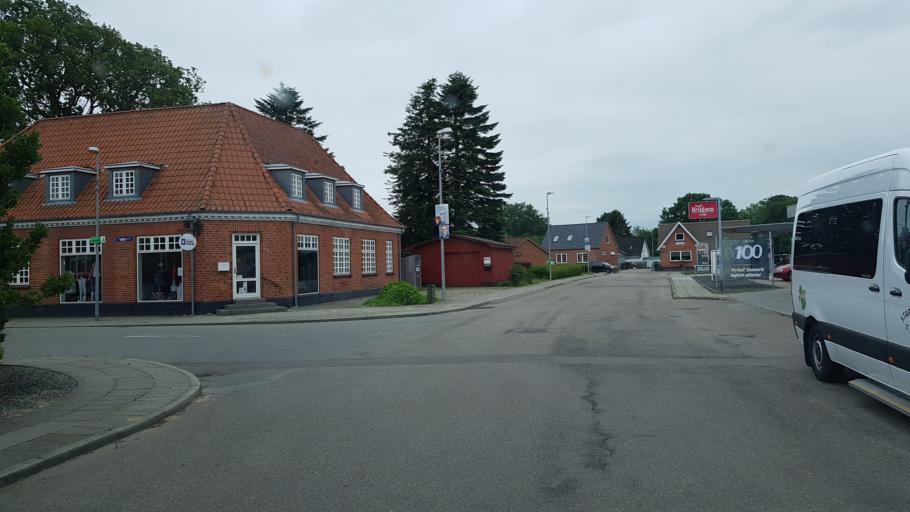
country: DK
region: South Denmark
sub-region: Varde Kommune
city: Olgod
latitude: 55.7050
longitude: 8.7501
